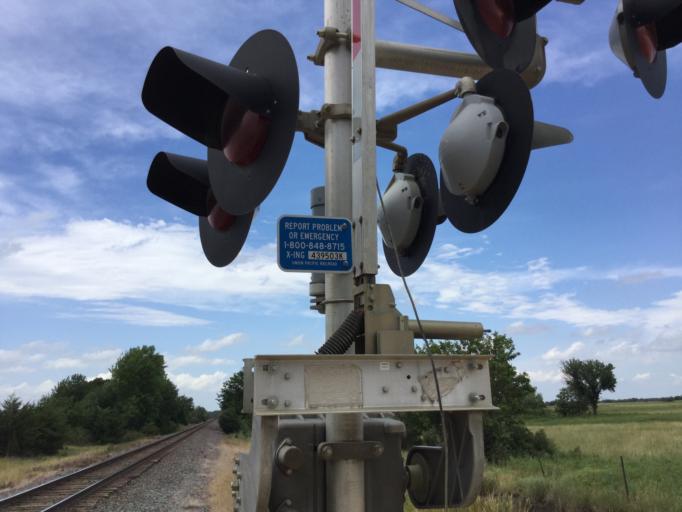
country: US
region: Kansas
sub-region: Woodson County
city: Yates Center
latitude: 38.0099
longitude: -95.6467
